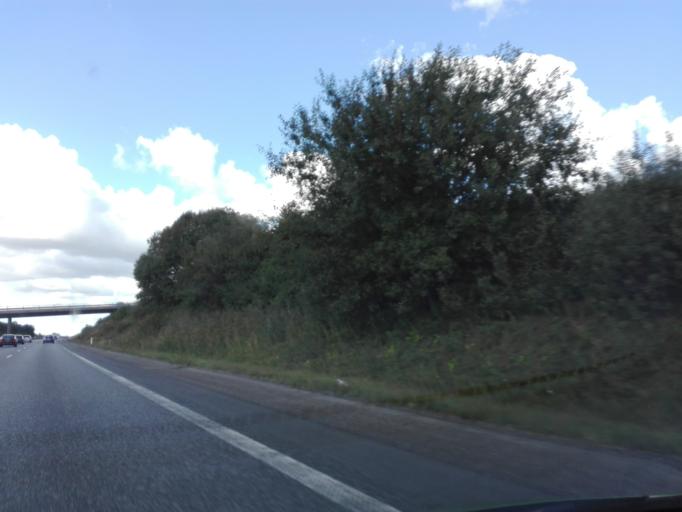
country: DK
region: North Denmark
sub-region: Mariagerfjord Kommune
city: Hobro
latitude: 56.5504
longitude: 9.8797
